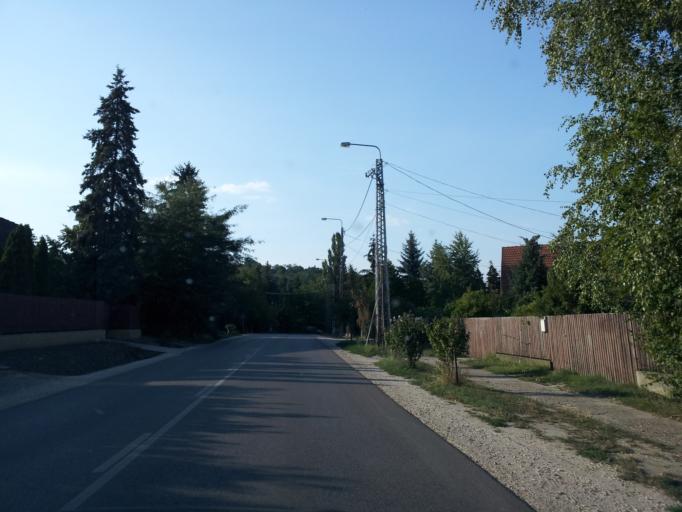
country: HU
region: Pest
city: Leanyfalu
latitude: 47.7265
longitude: 19.0884
